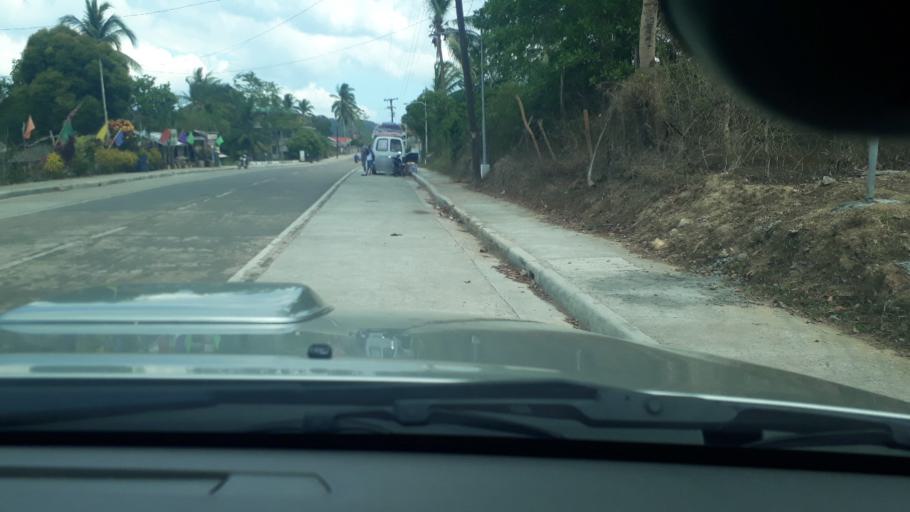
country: PH
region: Mimaropa
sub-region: Province of Palawan
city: Salvacion
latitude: 12.1297
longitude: 119.9375
